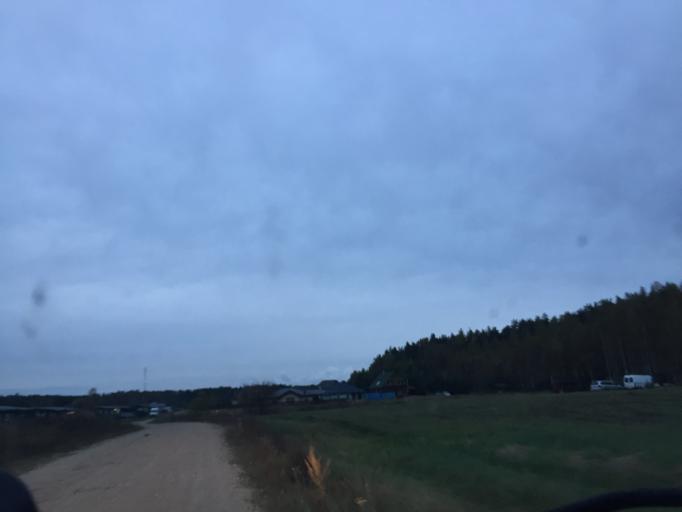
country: LV
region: Garkalne
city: Garkalne
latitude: 57.0839
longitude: 24.3793
